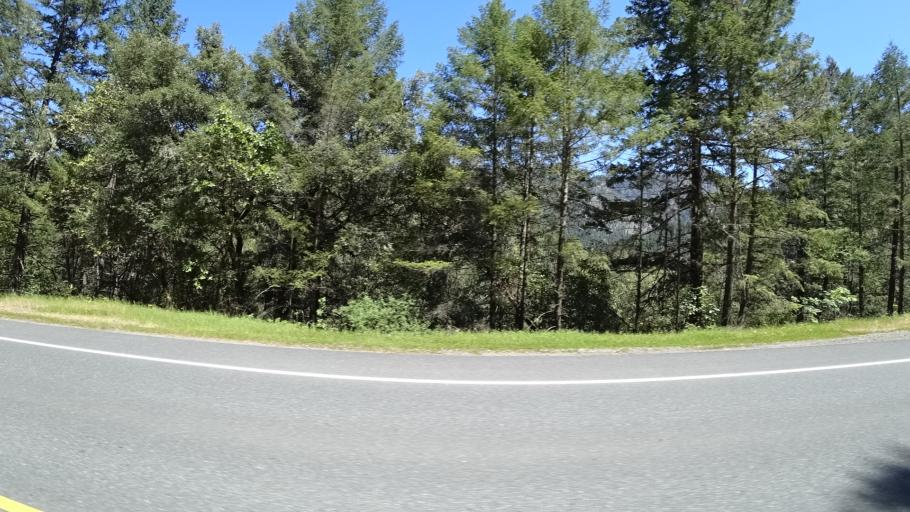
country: US
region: California
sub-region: Humboldt County
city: Willow Creek
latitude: 40.8619
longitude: -123.5130
